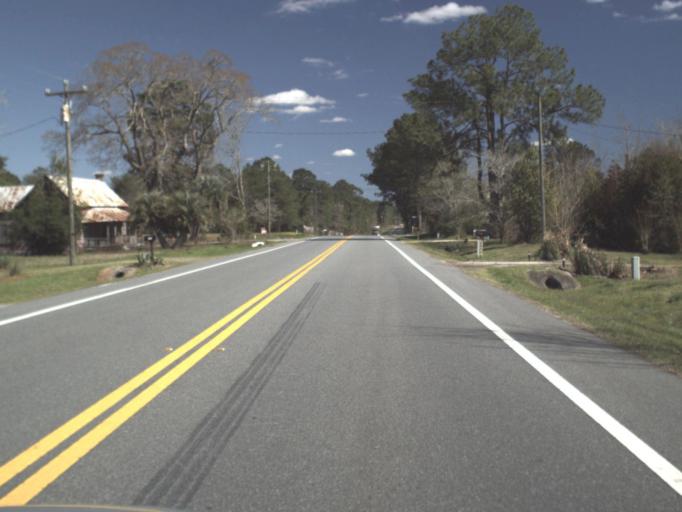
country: US
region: Florida
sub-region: Gadsden County
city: Chattahoochee
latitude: 30.7022
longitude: -84.7854
